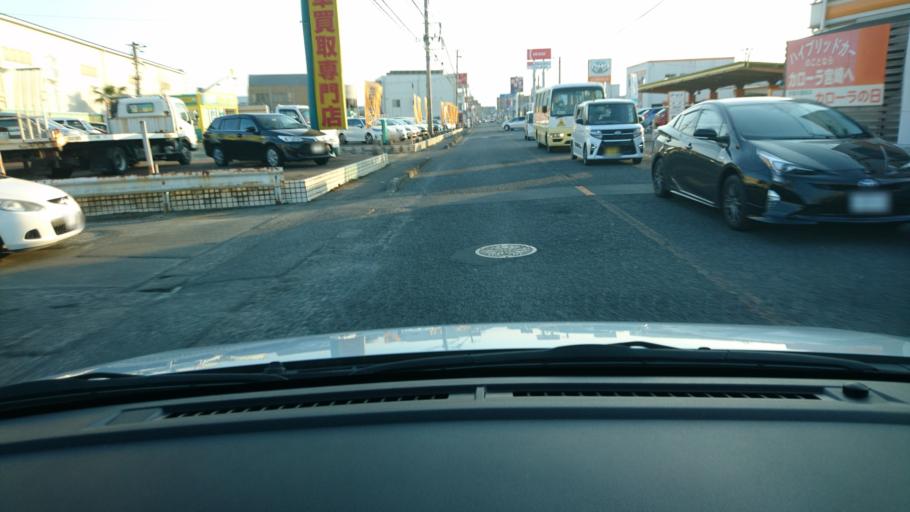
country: JP
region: Miyazaki
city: Miyazaki-shi
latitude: 31.9552
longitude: 131.4352
